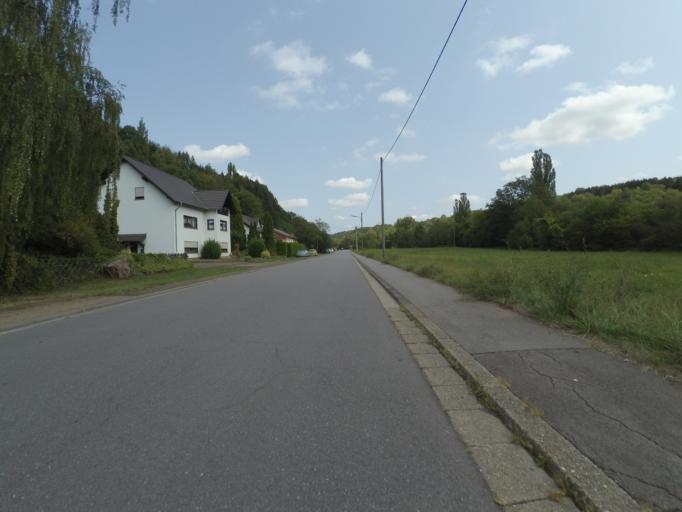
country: DE
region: Saarland
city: Merzig
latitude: 49.4534
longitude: 6.6675
